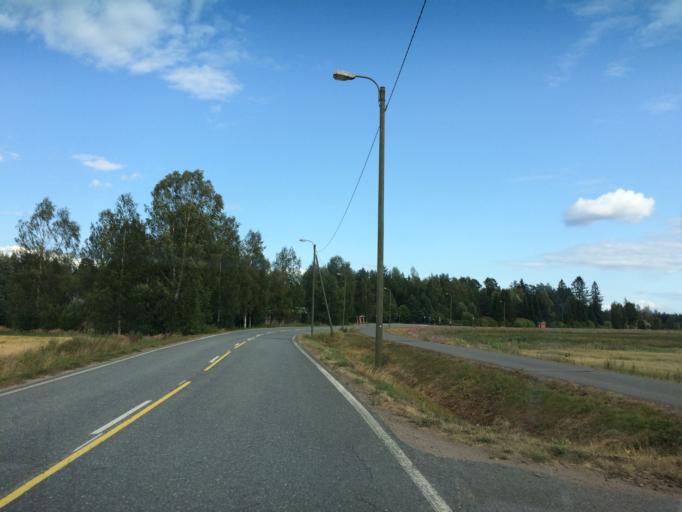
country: FI
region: Haeme
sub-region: Haemeenlinna
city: Tuulos
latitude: 61.0652
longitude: 24.6894
